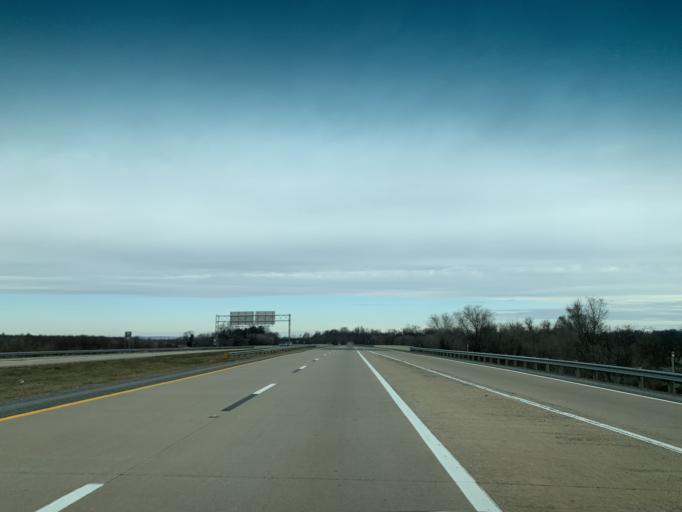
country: US
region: West Virginia
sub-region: Jefferson County
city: Ranson
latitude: 39.3638
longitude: -77.8675
